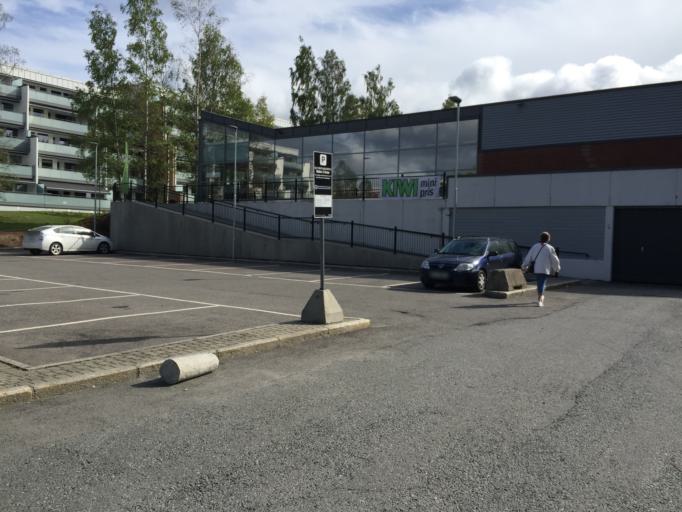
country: NO
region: Akershus
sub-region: Skedsmo
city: Lillestrom
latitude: 59.9309
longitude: 11.0344
